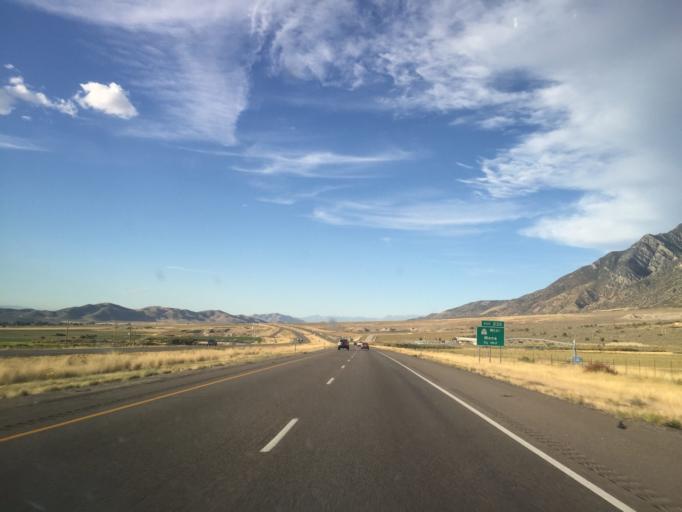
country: US
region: Utah
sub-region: Juab County
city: Mona
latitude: 39.8107
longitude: -111.8345
